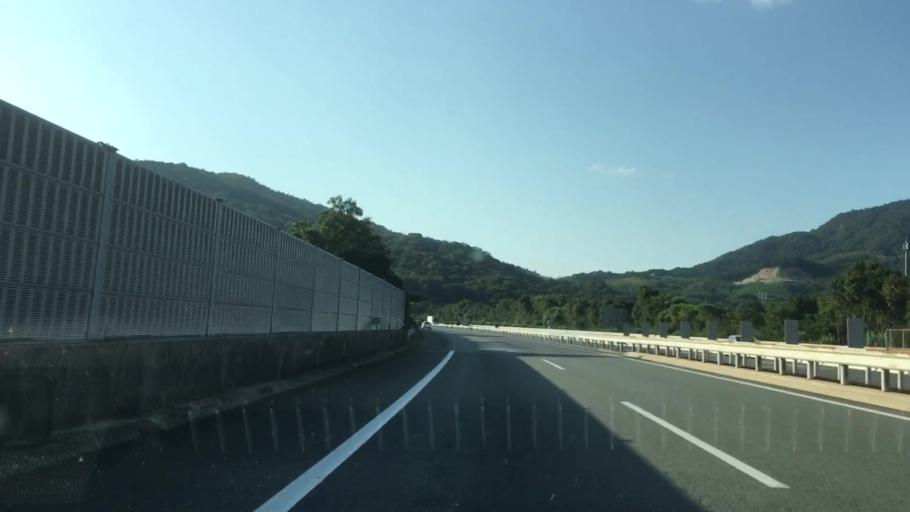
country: JP
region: Yamaguchi
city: Hofu
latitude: 34.0681
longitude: 131.6012
